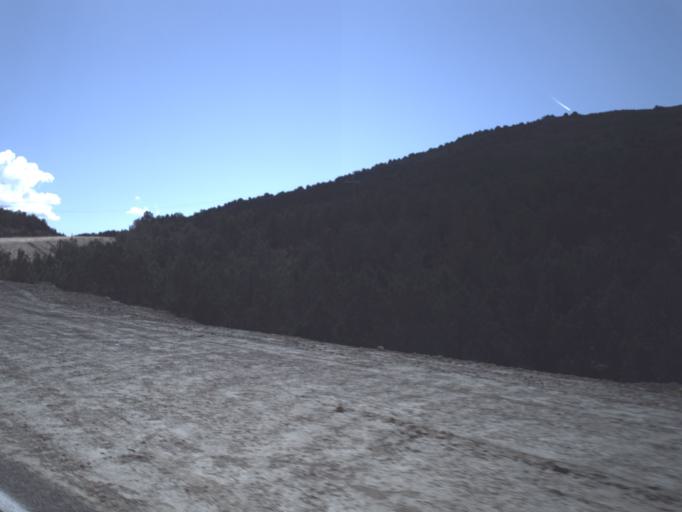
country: US
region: Utah
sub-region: Washington County
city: Enterprise
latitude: 37.5321
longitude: -113.6495
